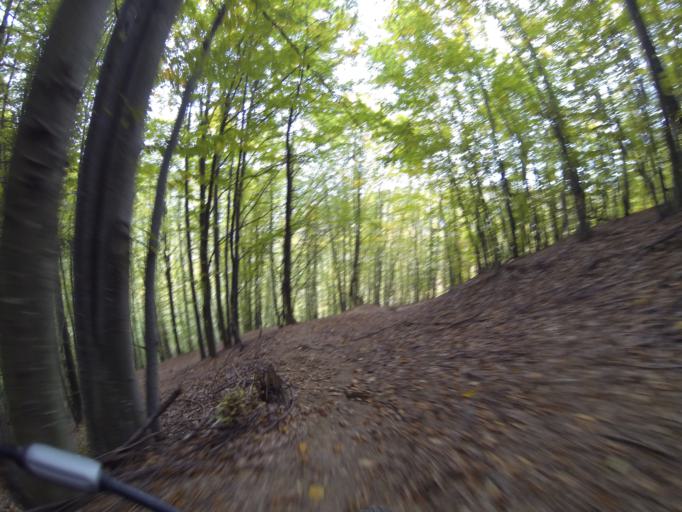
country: RO
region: Gorj
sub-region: Comuna Tismana
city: Sohodol
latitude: 45.0818
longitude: 22.8859
